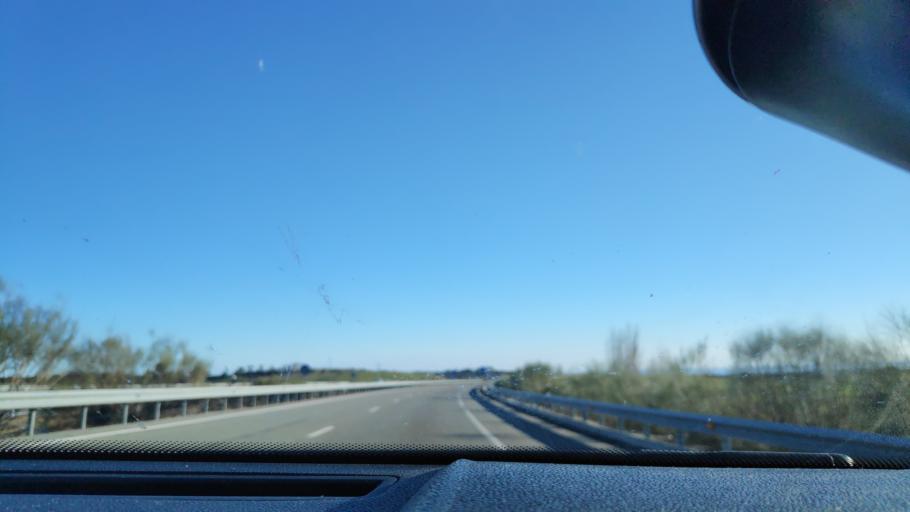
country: ES
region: Andalusia
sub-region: Provincia de Sevilla
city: El Ronquillo
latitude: 37.6338
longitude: -6.1499
